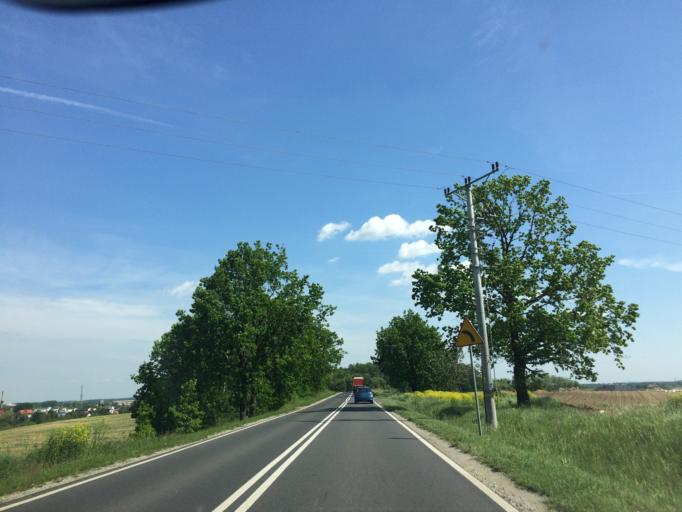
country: PL
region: Lower Silesian Voivodeship
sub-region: Powiat swidnicki
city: Swidnica
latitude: 50.8206
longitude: 16.5000
